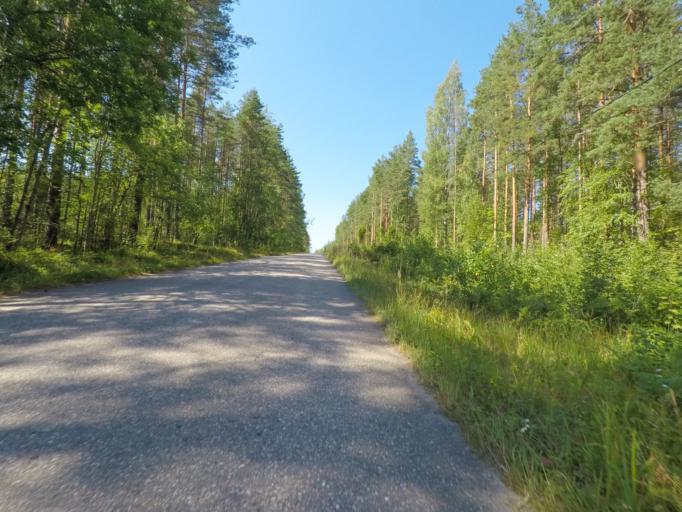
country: FI
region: Southern Savonia
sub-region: Mikkeli
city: Puumala
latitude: 61.4226
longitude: 28.1342
